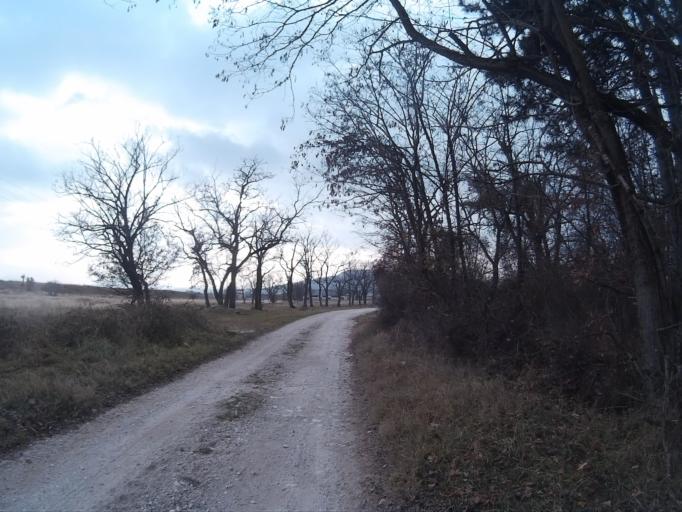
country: HU
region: Veszprem
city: Tapolca
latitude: 46.9412
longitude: 17.4849
